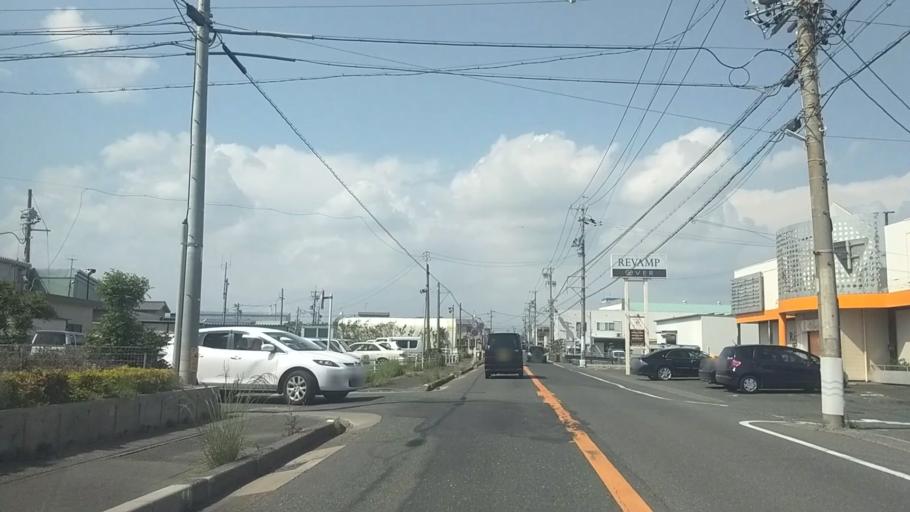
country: JP
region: Shizuoka
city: Hamamatsu
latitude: 34.6841
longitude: 137.7111
